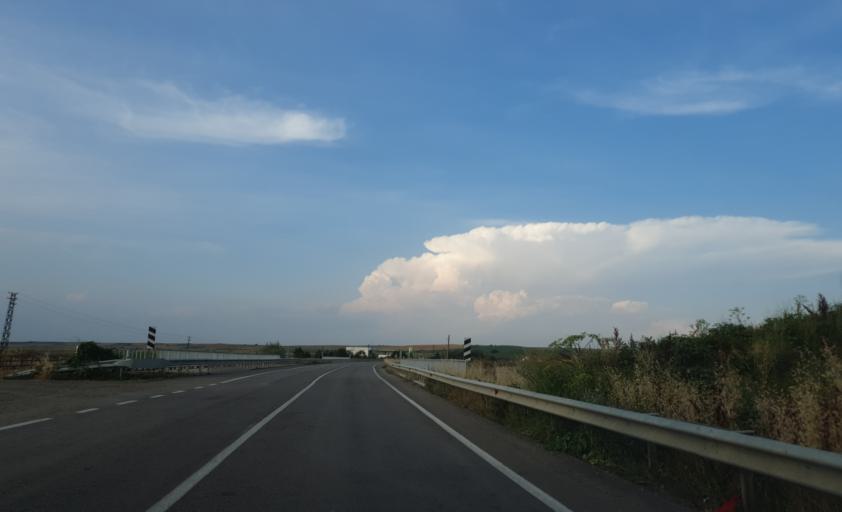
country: TR
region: Tekirdag
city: Hayrabolu
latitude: 41.2324
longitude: 27.1239
